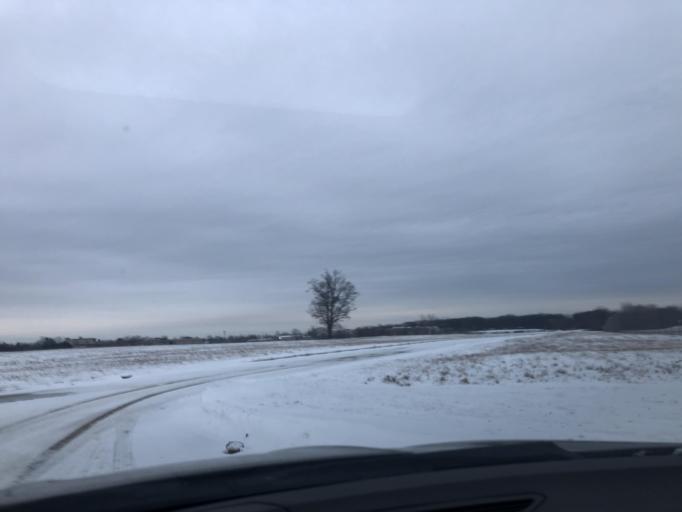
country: US
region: Michigan
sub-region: Ingham County
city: Edgemont Park
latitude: 42.7754
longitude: -84.5756
